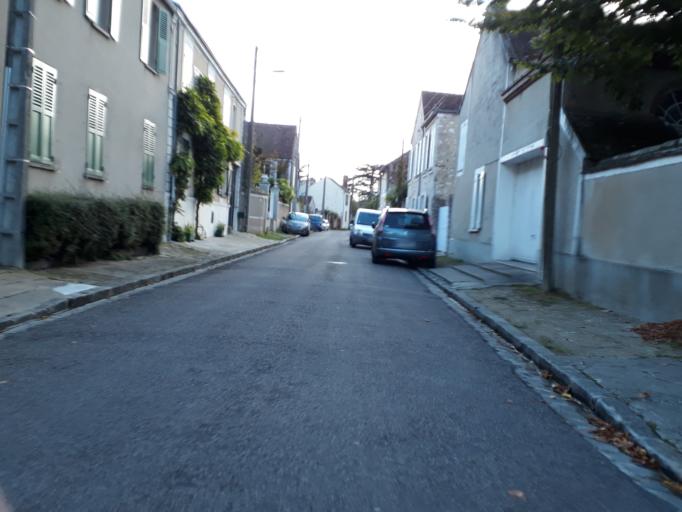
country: FR
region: Ile-de-France
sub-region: Departement de Seine-et-Marne
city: Bois-le-Roi
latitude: 48.4673
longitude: 2.7032
